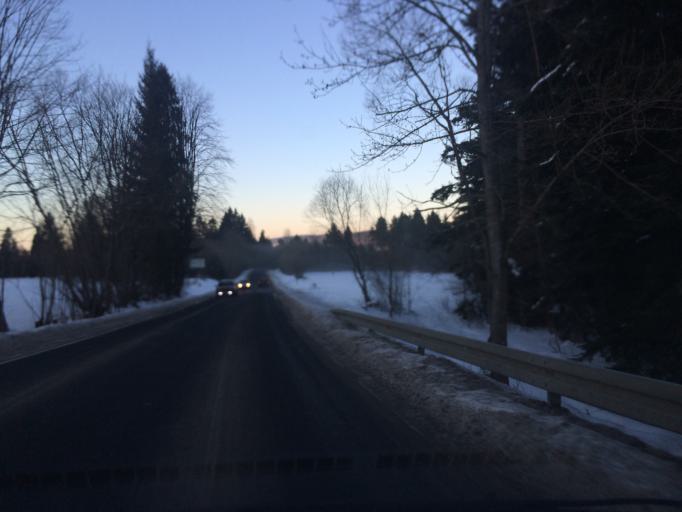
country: PL
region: Subcarpathian Voivodeship
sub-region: Powiat bieszczadzki
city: Czarna
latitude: 49.3015
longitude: 22.6697
